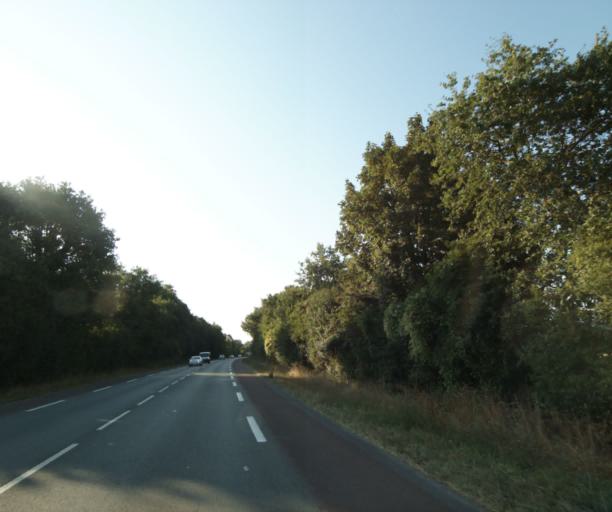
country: FR
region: Poitou-Charentes
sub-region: Departement de la Charente-Maritime
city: Cabariot
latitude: 45.9478
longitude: -0.8667
